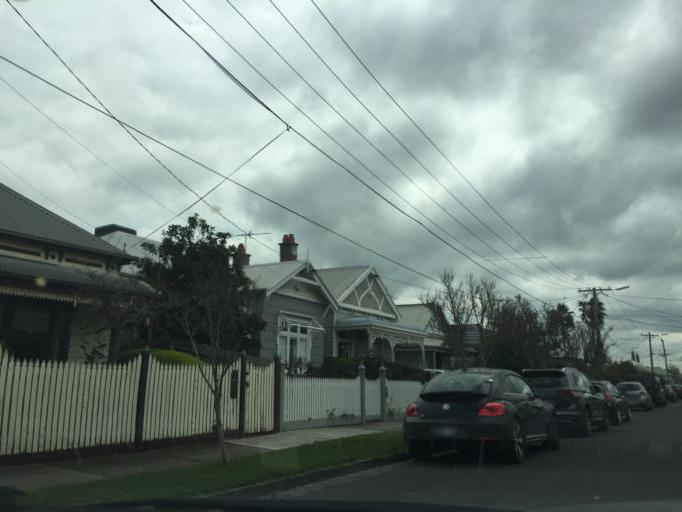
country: AU
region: Victoria
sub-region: Maribyrnong
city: Seddon
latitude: -37.8114
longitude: 144.8886
